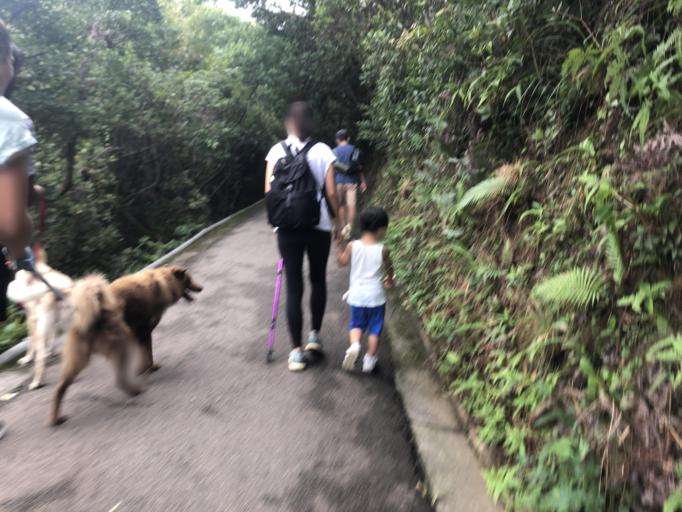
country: HK
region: Central and Western
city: Central
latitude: 22.2770
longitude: 114.1369
